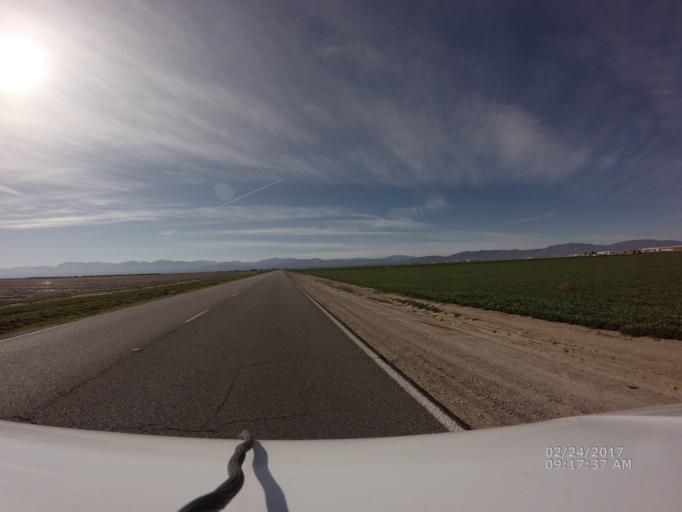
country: US
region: California
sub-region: Los Angeles County
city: Palmdale
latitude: 34.6510
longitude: -118.0410
